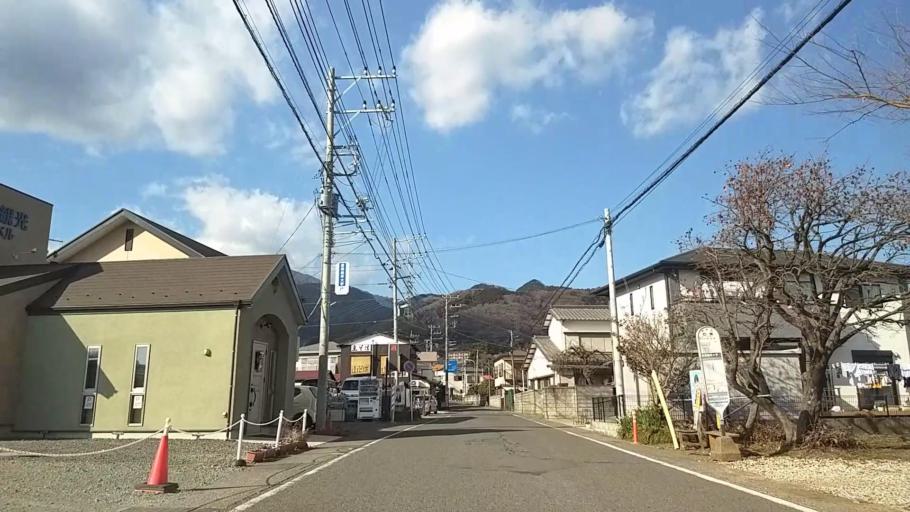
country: JP
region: Kanagawa
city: Isehara
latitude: 35.4128
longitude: 139.2855
